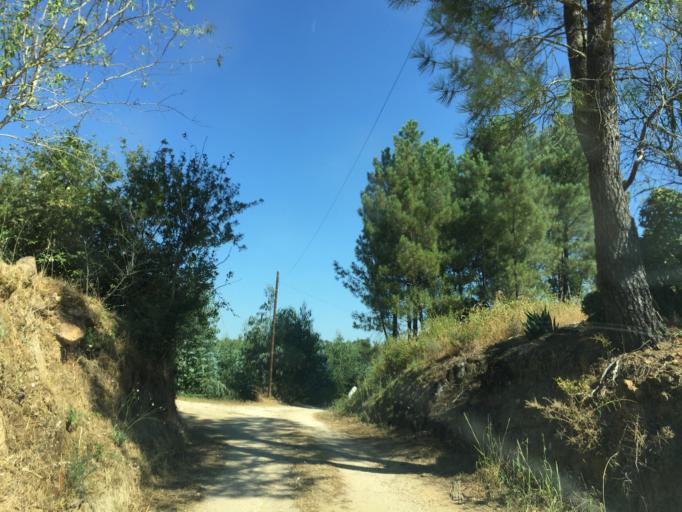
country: PT
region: Santarem
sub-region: Tomar
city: Tomar
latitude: 39.6065
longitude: -8.3483
